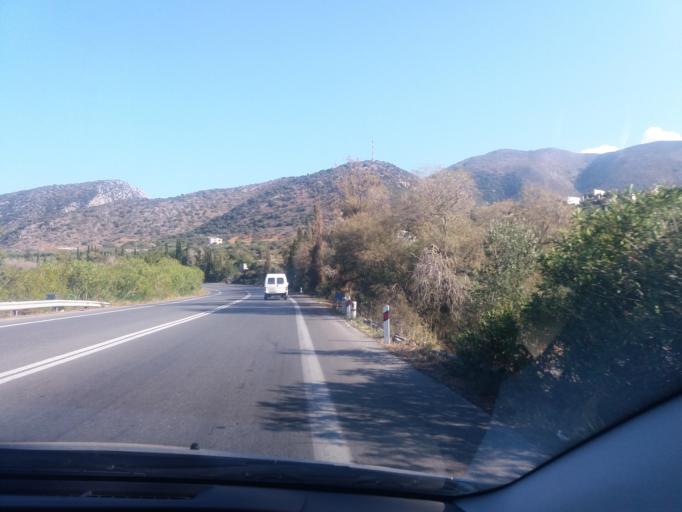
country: GR
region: Crete
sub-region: Nomos Lasithiou
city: Sision
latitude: 35.2926
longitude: 25.5200
